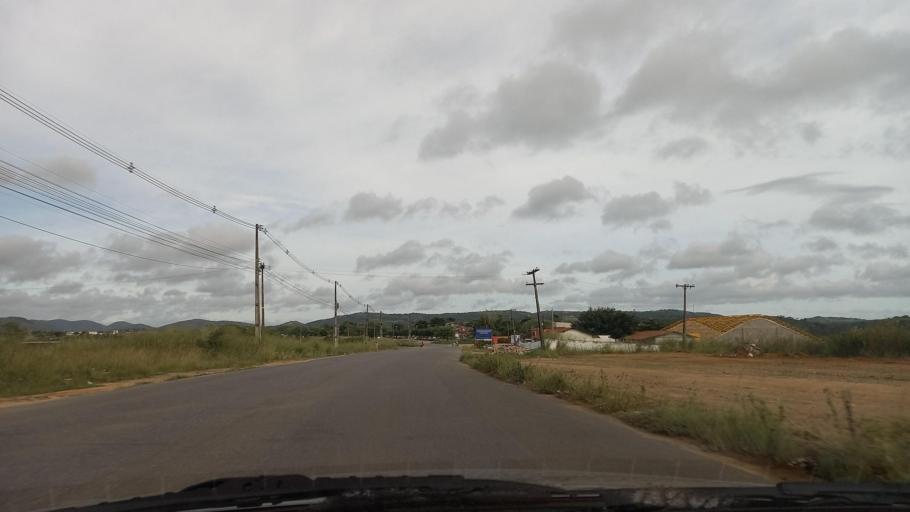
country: BR
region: Pernambuco
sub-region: Vitoria De Santo Antao
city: Vitoria de Santo Antao
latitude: -8.1259
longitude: -35.3436
